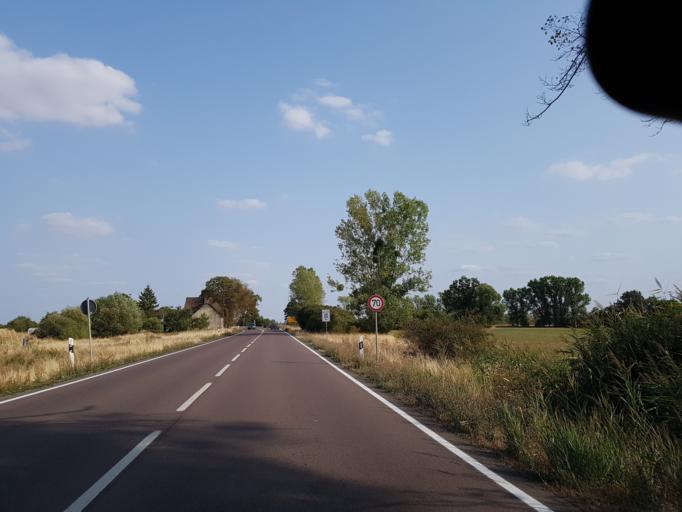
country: DE
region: Saxony-Anhalt
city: Kemberg
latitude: 51.8082
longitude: 12.6475
